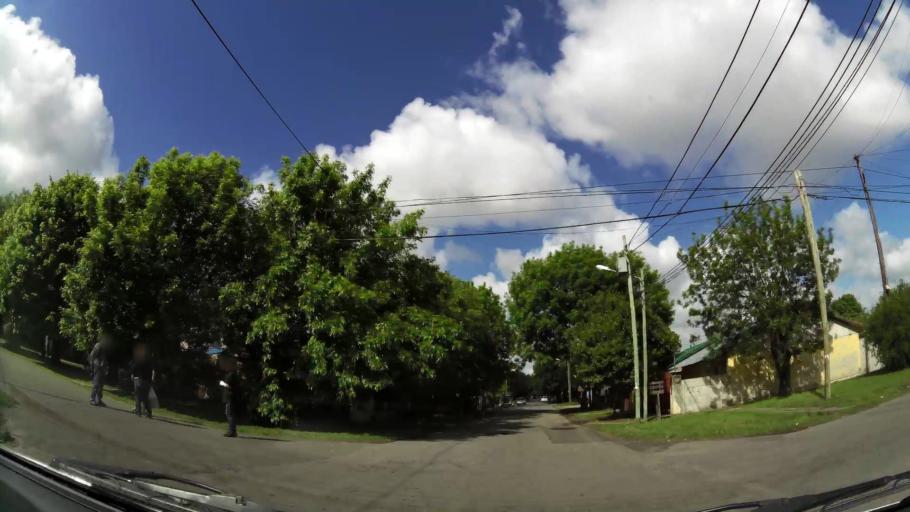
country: AR
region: Buenos Aires
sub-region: Partido de Quilmes
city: Quilmes
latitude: -34.7966
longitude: -58.1563
